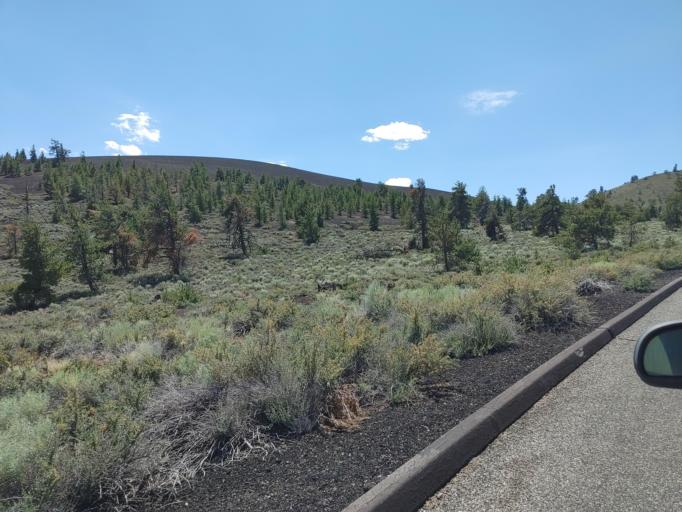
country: US
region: Idaho
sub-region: Butte County
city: Arco
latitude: 43.4469
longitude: -113.5506
